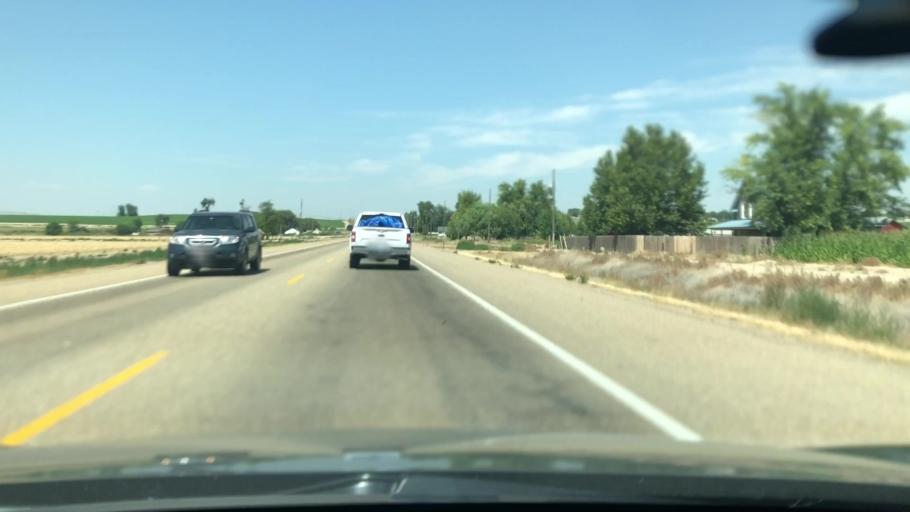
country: US
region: Idaho
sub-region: Canyon County
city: Parma
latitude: 43.8119
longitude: -116.9543
